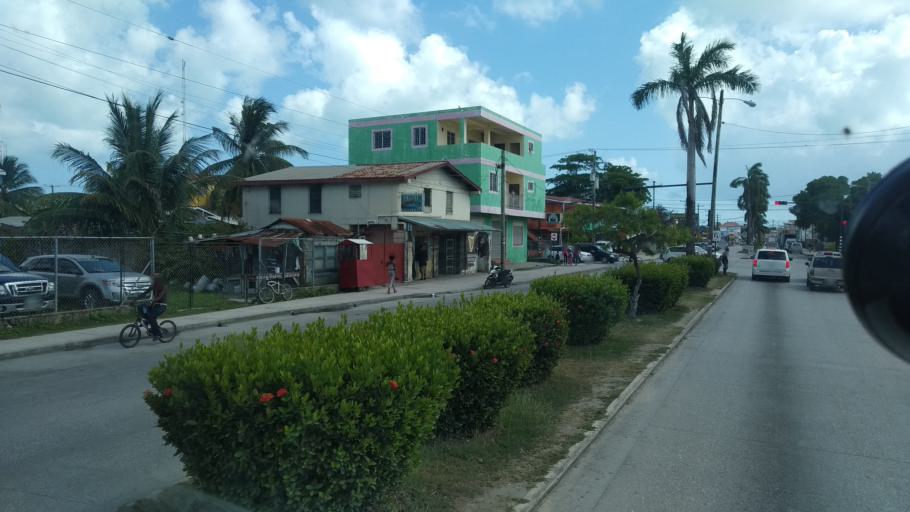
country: BZ
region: Belize
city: Belize City
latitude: 17.4987
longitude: -88.1990
